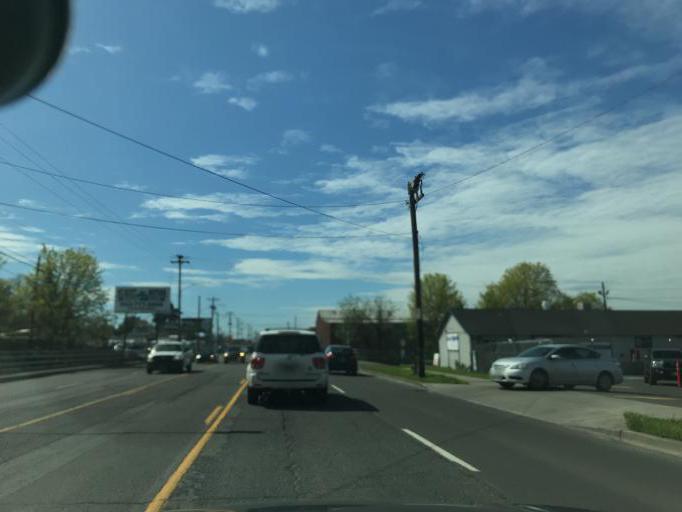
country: US
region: Oregon
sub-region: Multnomah County
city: Lents
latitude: 45.4639
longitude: -122.5791
